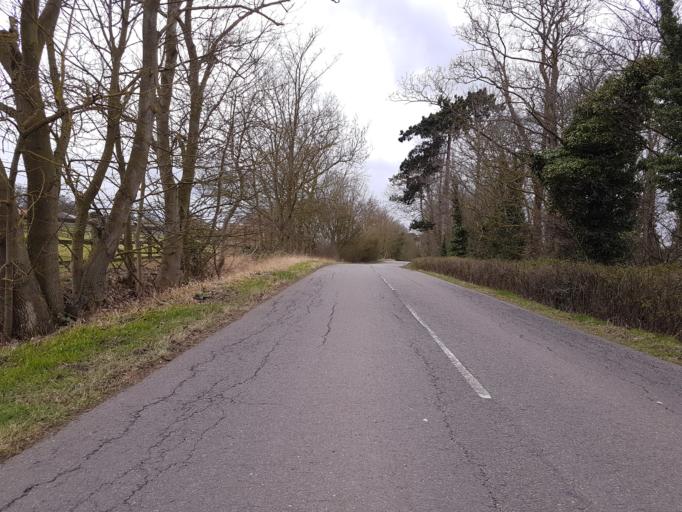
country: GB
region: England
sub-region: Cambridgeshire
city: Girton
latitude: 52.2164
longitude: 0.0628
